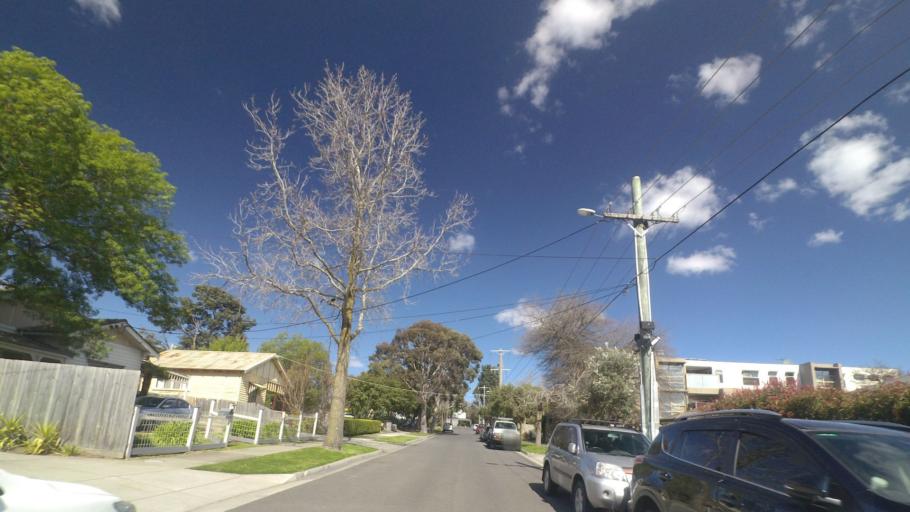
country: AU
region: Victoria
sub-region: Knox
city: Bayswater
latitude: -37.8402
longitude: 145.2619
